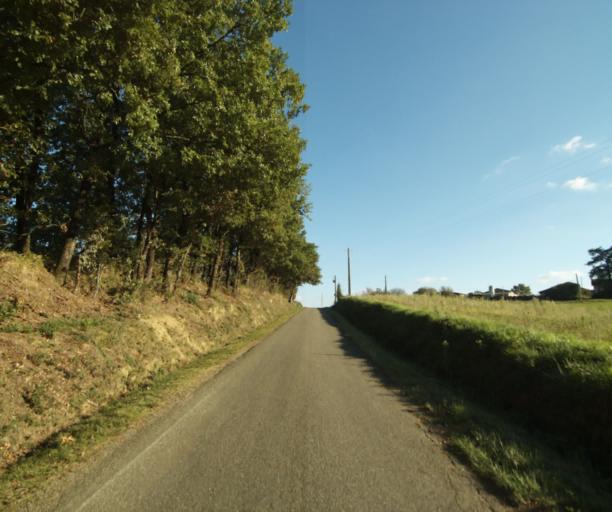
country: FR
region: Midi-Pyrenees
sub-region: Departement du Gers
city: Eauze
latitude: 43.7837
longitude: 0.1501
